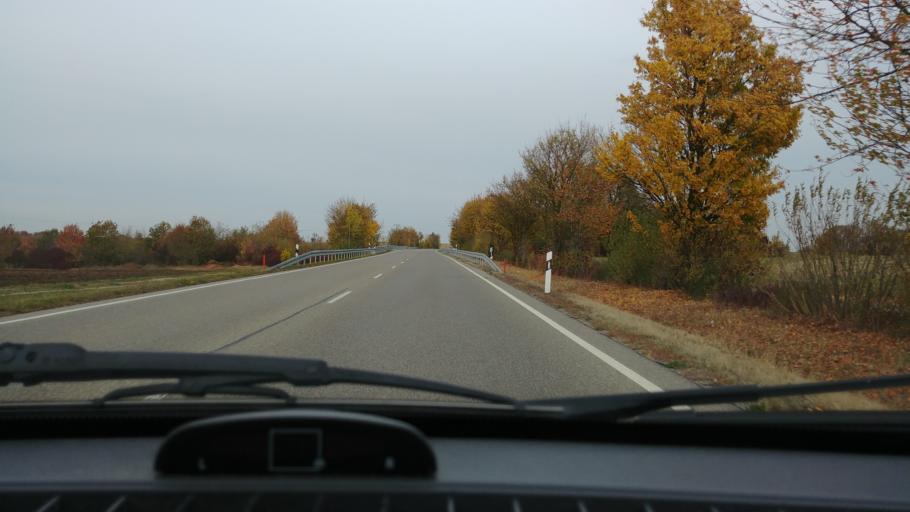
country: DE
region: Baden-Wuerttemberg
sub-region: Regierungsbezirk Stuttgart
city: Satteldorf
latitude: 49.1653
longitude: 10.0726
